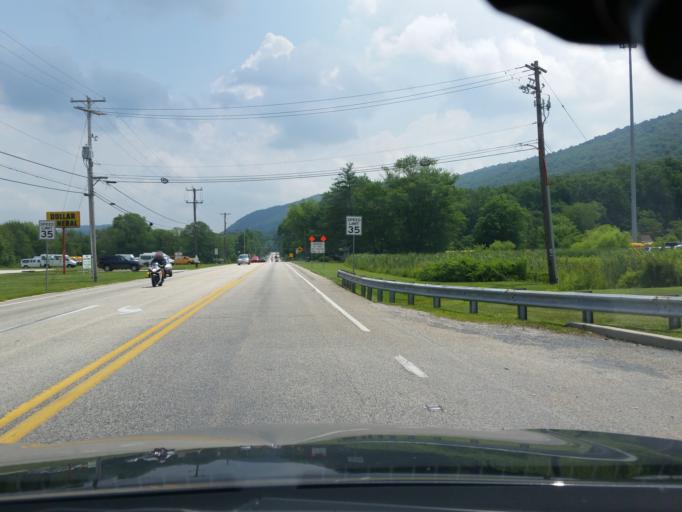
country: US
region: Pennsylvania
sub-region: Perry County
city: Duncannon
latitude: 40.3553
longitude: -76.9865
